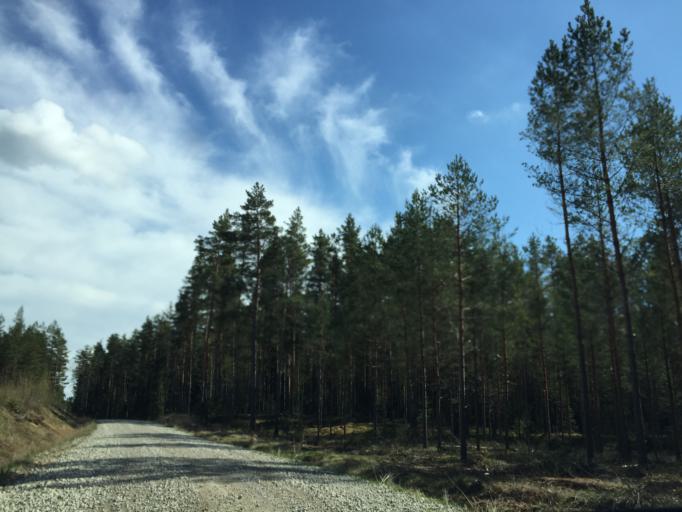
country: LV
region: Strenci
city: Strenci
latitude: 57.5945
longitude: 25.6923
